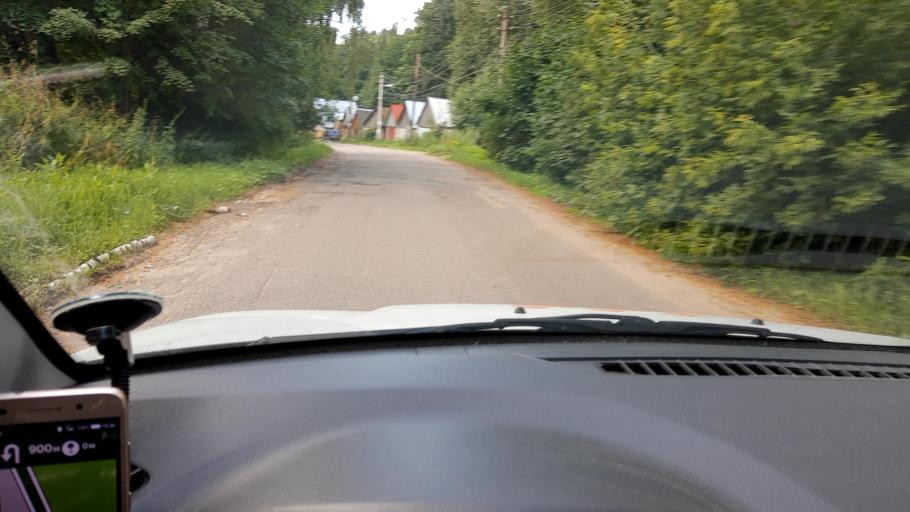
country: RU
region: Nizjnij Novgorod
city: Afonino
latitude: 56.2056
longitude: 44.0230
